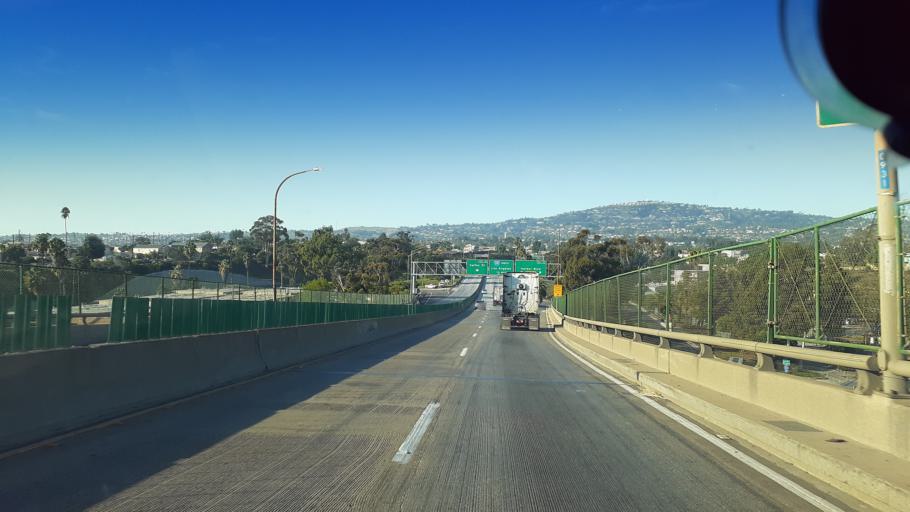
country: US
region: California
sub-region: Los Angeles County
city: San Pedro
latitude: 33.7499
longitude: -118.2802
